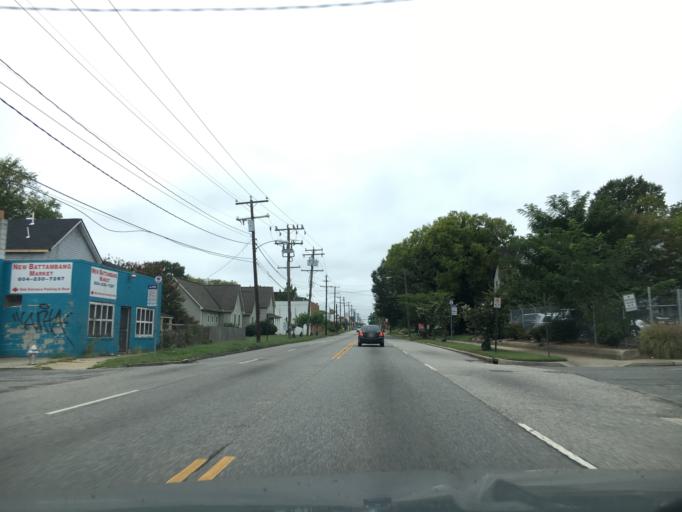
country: US
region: Virginia
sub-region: City of Richmond
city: Richmond
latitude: 37.5112
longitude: -77.4594
